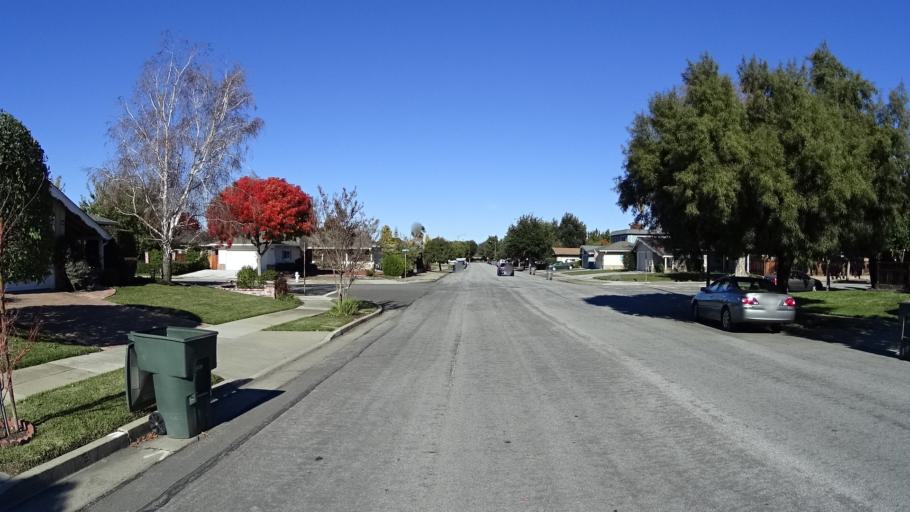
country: US
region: California
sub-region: Santa Clara County
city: Cupertino
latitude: 37.3382
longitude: -122.0026
